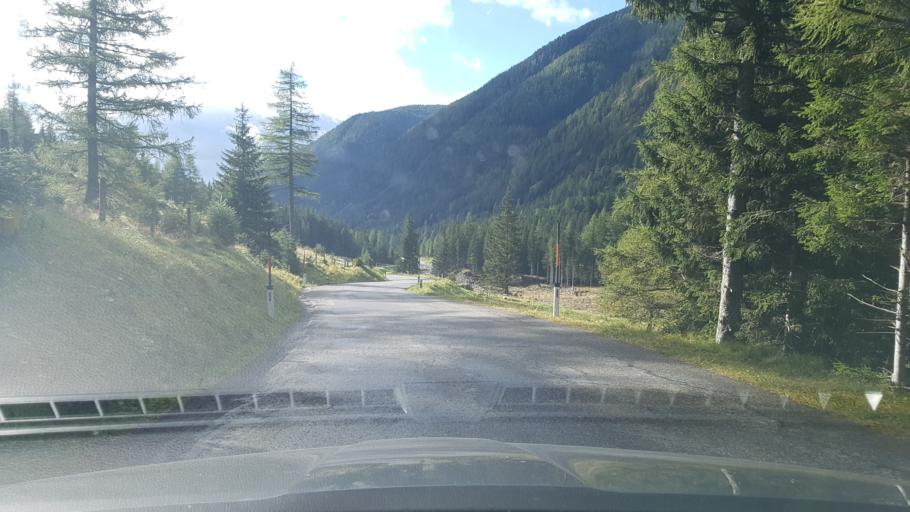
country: AT
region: Styria
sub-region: Politischer Bezirk Murau
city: Schoder
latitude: 47.2487
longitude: 14.0819
